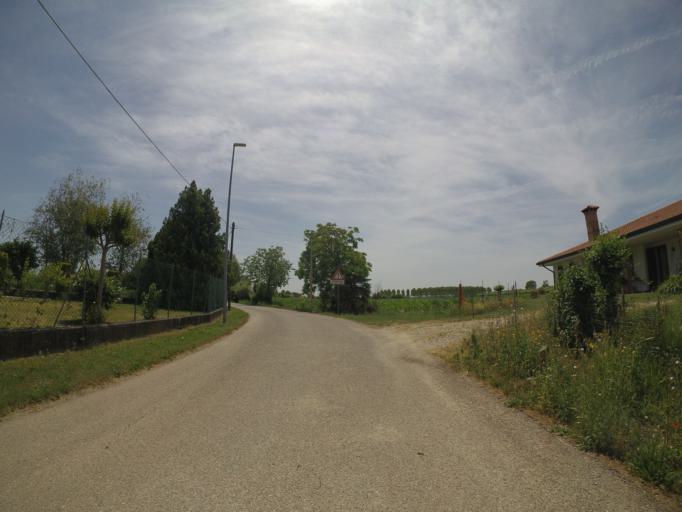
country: IT
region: Friuli Venezia Giulia
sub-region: Provincia di Udine
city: Camino al Tagliamento
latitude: 45.9143
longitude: 12.9527
